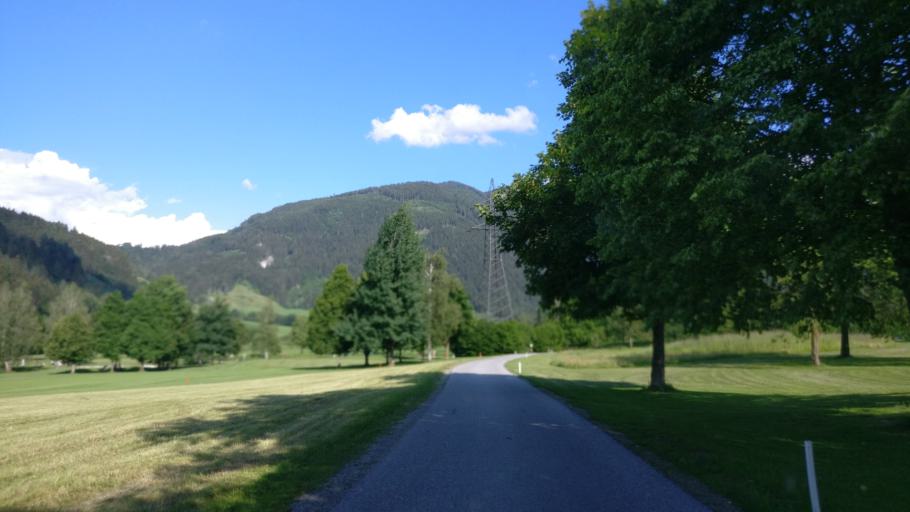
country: AT
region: Salzburg
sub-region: Politischer Bezirk Sankt Johann im Pongau
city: Radstadt
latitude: 47.3735
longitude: 13.4742
